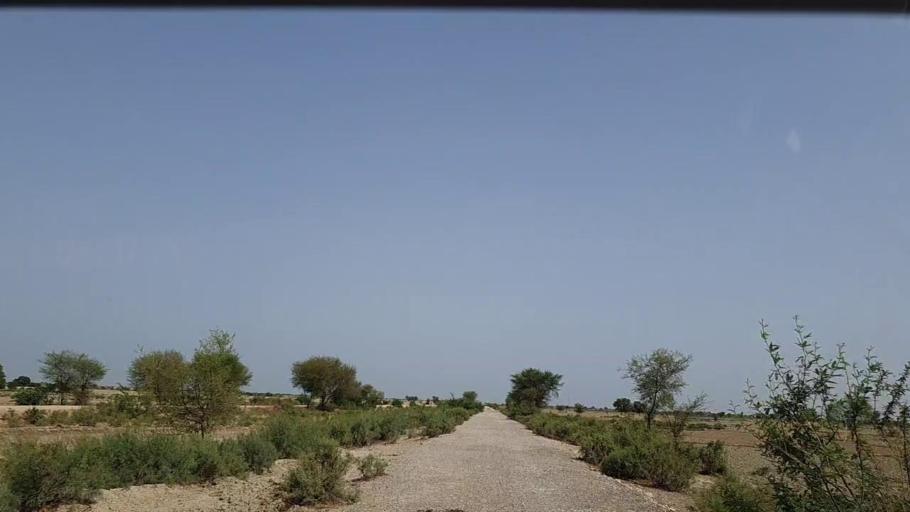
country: PK
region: Sindh
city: Johi
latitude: 26.7505
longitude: 67.6711
